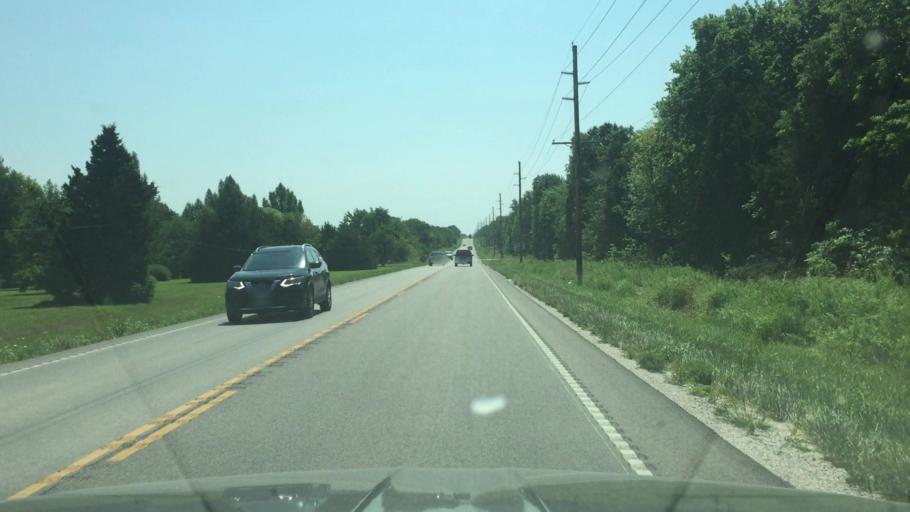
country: US
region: Missouri
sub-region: Morgan County
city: Versailles
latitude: 38.4012
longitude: -92.7439
